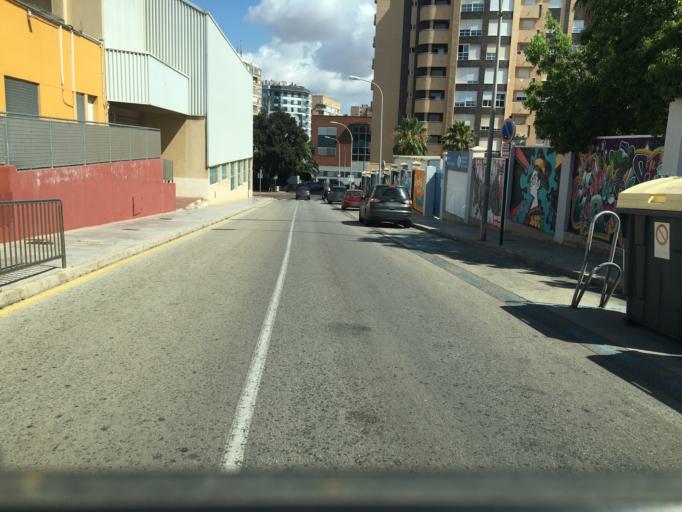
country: ES
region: Murcia
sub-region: Murcia
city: Cartagena
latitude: 37.6049
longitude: -0.9808
